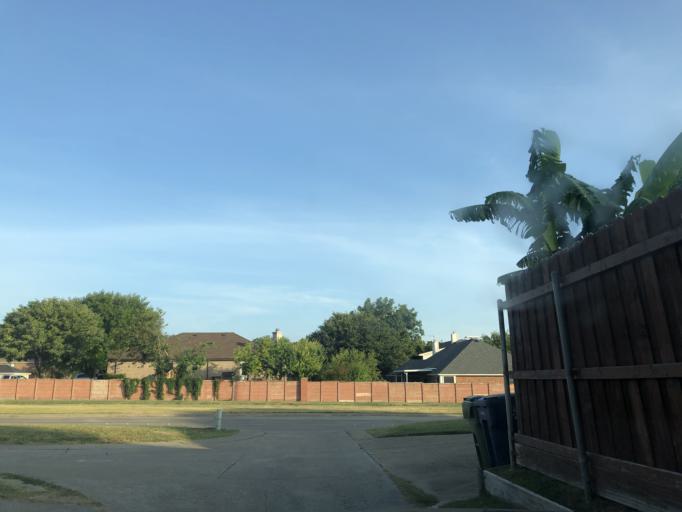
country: US
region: Texas
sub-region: Dallas County
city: Garland
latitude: 32.8529
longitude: -96.6233
